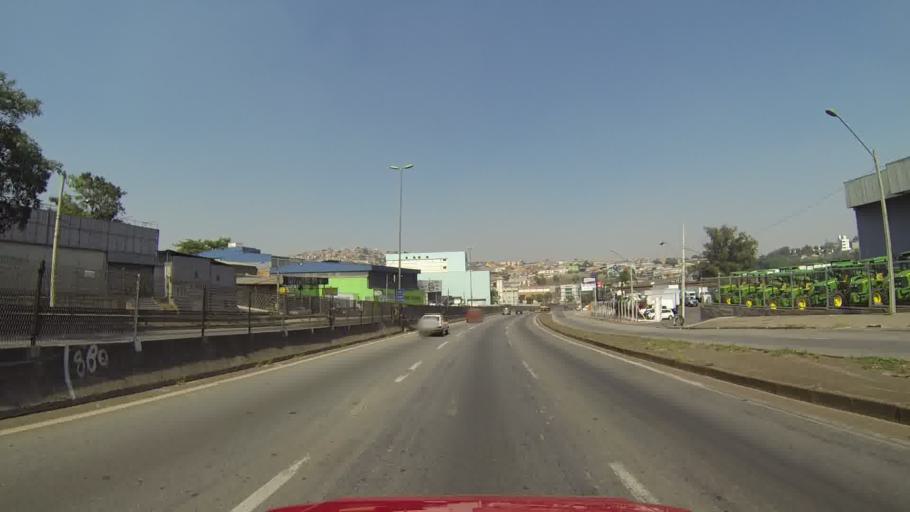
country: BR
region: Minas Gerais
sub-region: Contagem
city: Contagem
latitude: -19.9640
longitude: -44.0440
